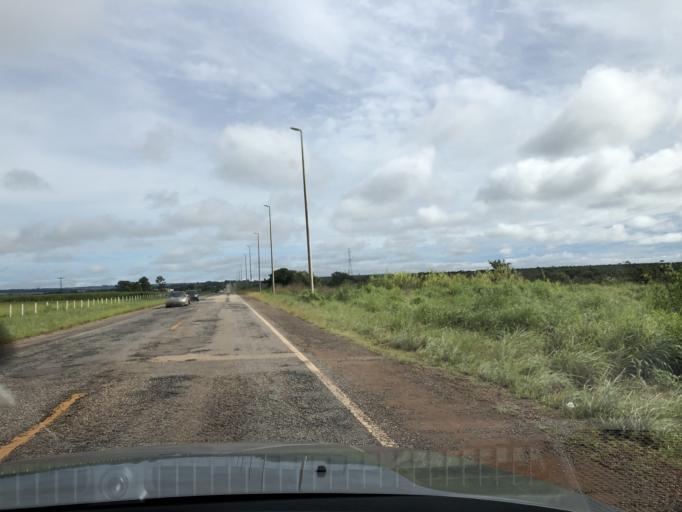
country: BR
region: Federal District
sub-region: Brasilia
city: Brasilia
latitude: -15.7216
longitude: -48.0866
